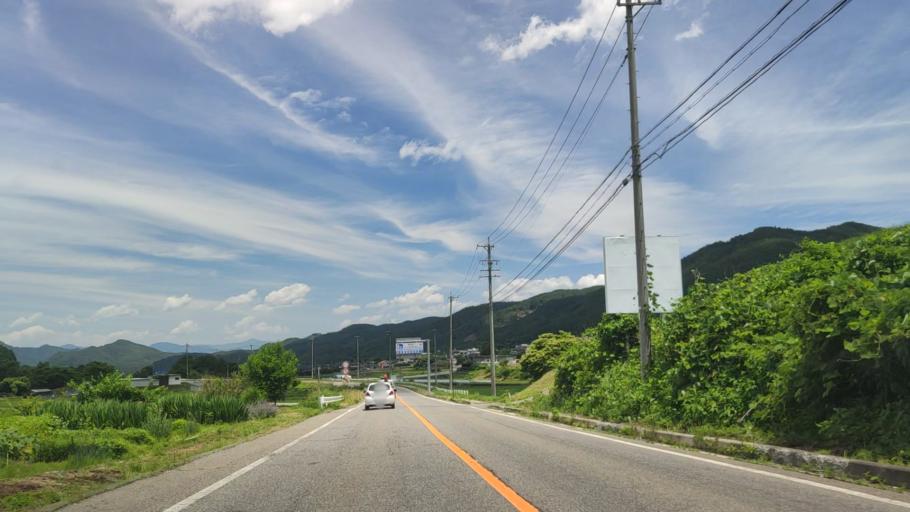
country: JP
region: Nagano
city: Kamimaruko
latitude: 36.2494
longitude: 138.2627
